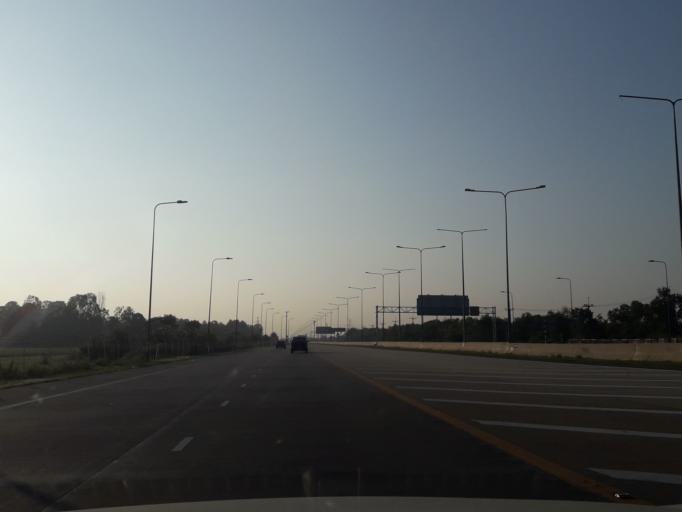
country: TH
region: Phra Nakhon Si Ayutthaya
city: Bang Pa-in
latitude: 14.1440
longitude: 100.5579
